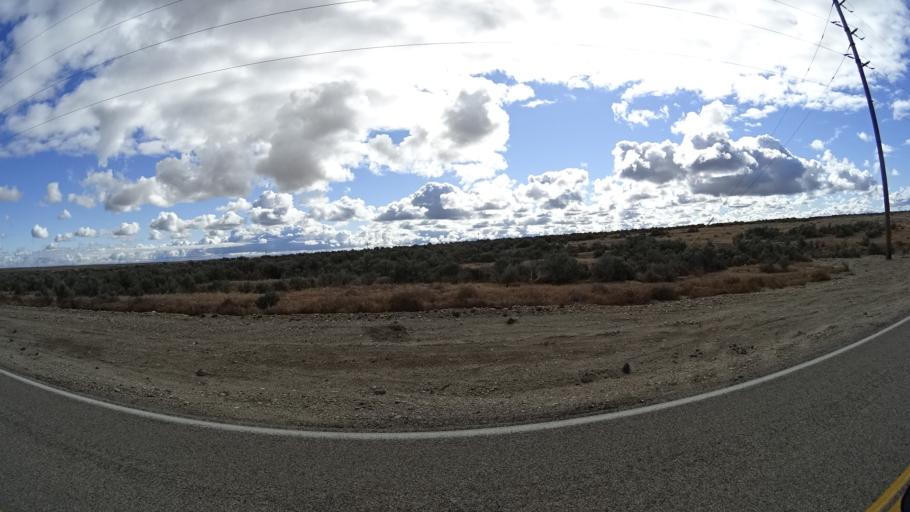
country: US
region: Idaho
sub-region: Owyhee County
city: Murphy
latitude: 43.2503
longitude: -116.3719
